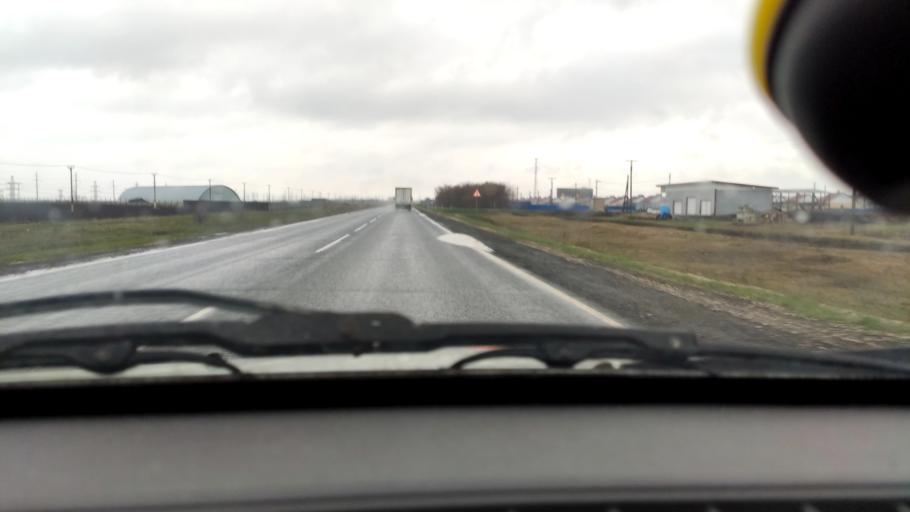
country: RU
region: Samara
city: Povolzhskiy
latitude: 53.6425
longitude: 49.6646
